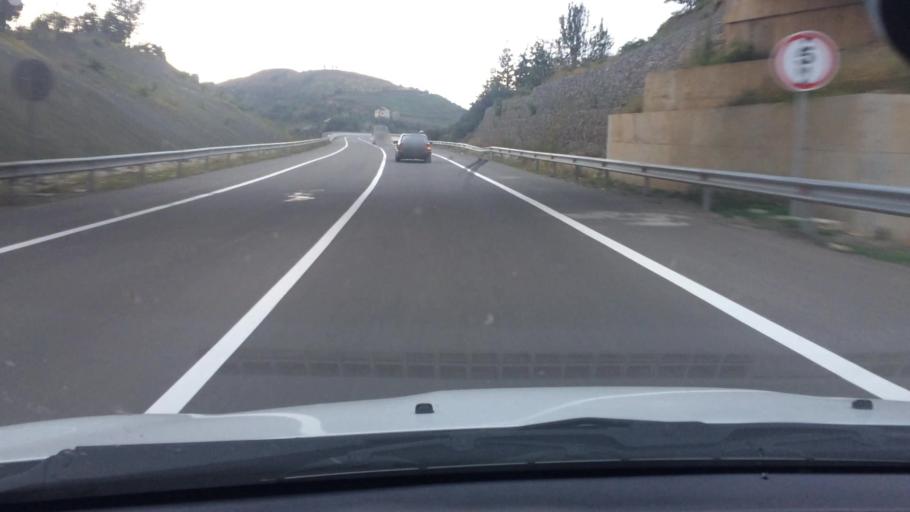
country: GE
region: Ajaria
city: Makhinjauri
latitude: 41.7184
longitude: 41.7514
